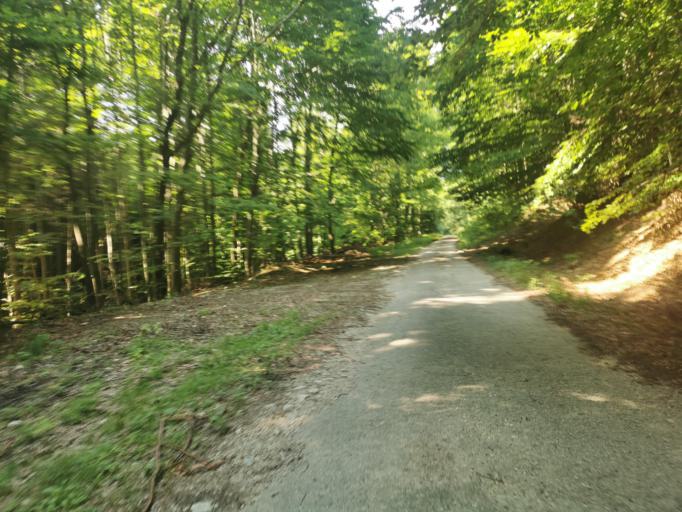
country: SK
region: Trenciansky
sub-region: Okres Myjava
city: Myjava
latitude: 48.8120
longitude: 17.5660
